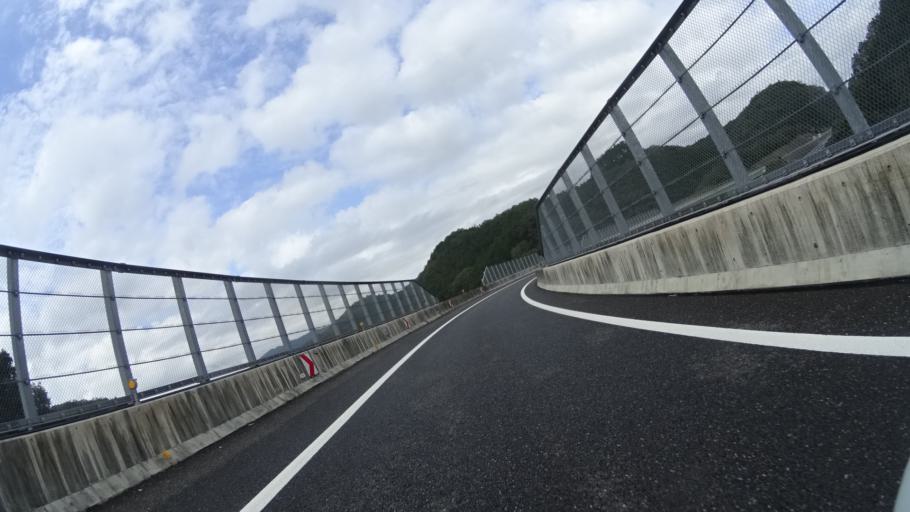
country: JP
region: Hyogo
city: Yamazakicho-nakabirose
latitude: 35.0214
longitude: 134.3901
